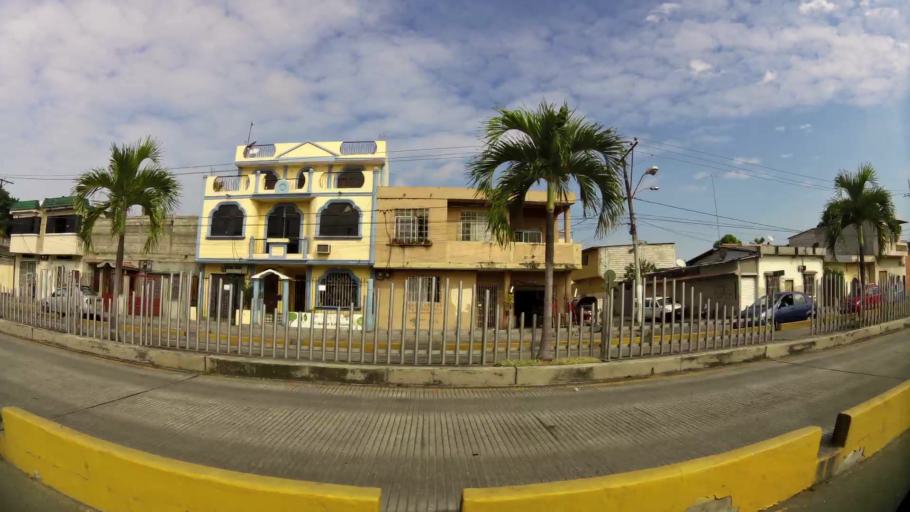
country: EC
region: Guayas
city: Guayaquil
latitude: -2.2553
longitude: -79.8793
